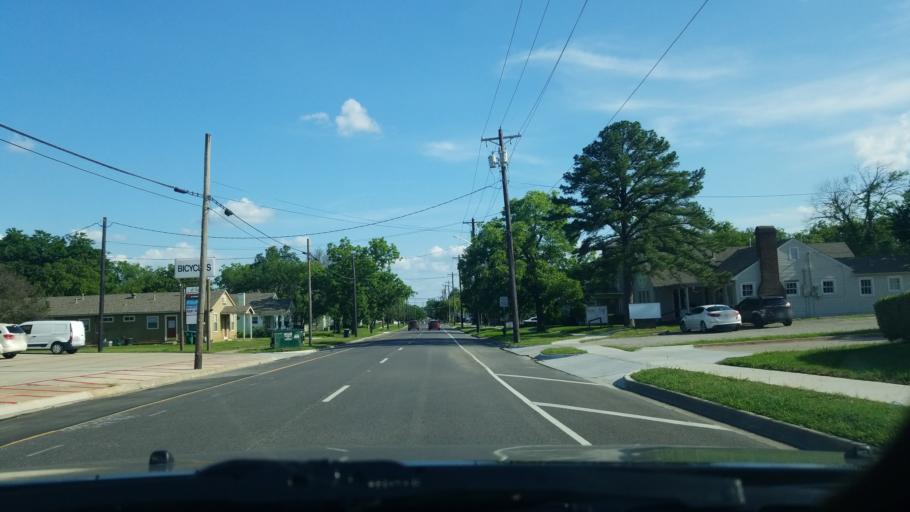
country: US
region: Texas
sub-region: Denton County
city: Denton
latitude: 33.2293
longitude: -97.1335
